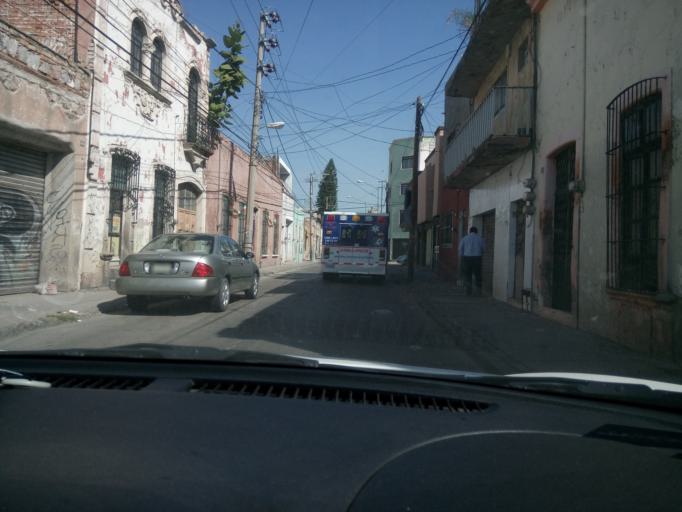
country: MX
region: Guanajuato
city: Leon
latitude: 21.1290
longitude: -101.6799
